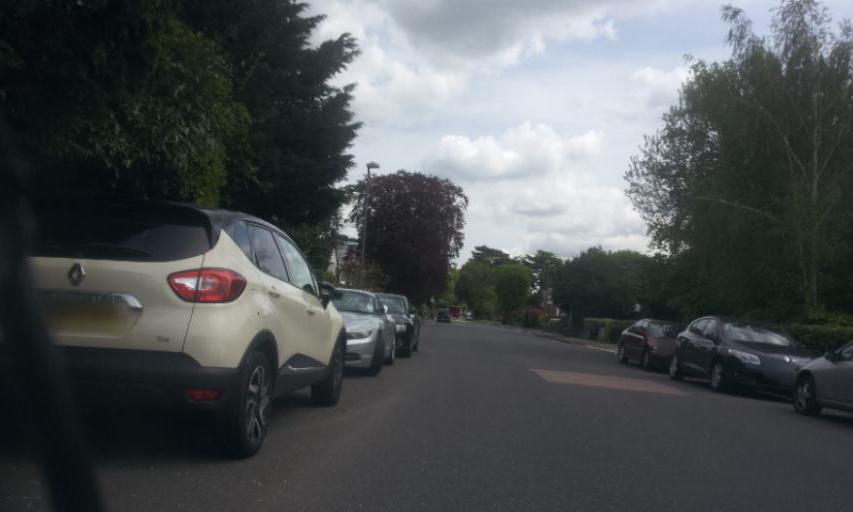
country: GB
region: England
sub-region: Greater London
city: Bromley
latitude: 51.3989
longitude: 0.0435
